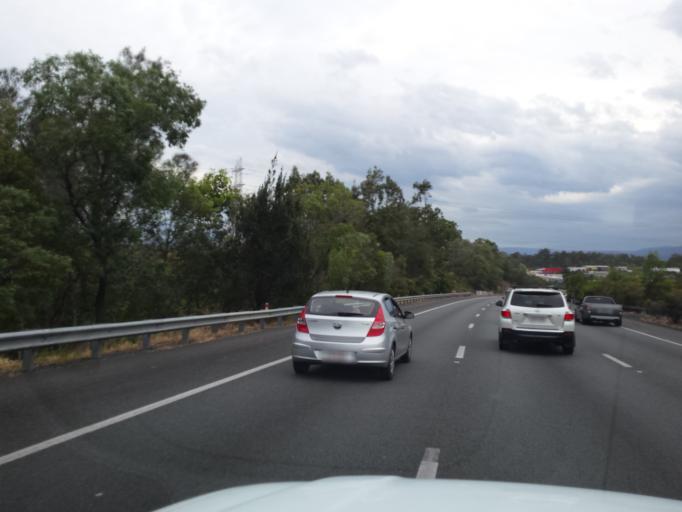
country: AU
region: Queensland
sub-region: Gold Coast
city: Nerang
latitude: -27.9749
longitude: 153.3460
